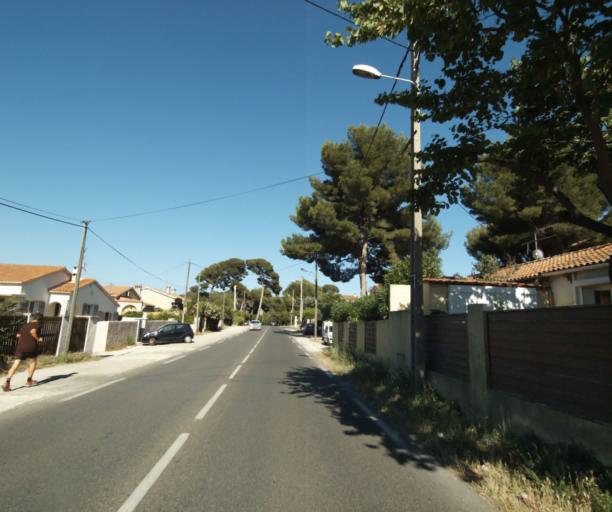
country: FR
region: Provence-Alpes-Cote d'Azur
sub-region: Departement du Var
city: La Garde
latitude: 43.1076
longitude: 5.9867
